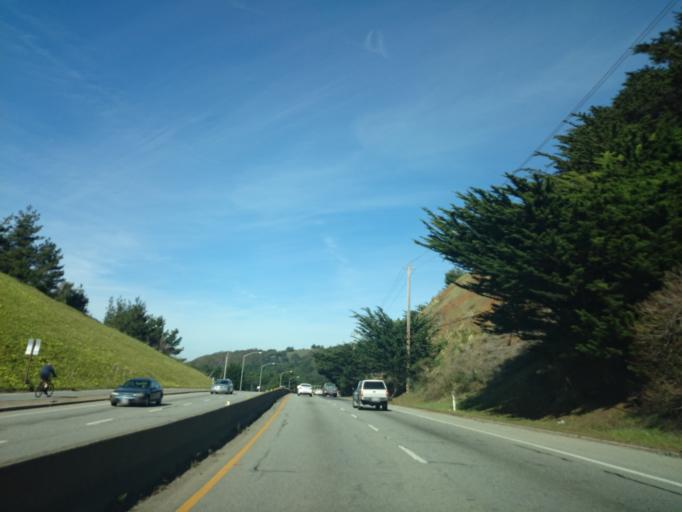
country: US
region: California
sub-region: San Mateo County
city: Pacifica
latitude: 37.6167
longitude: -122.4853
